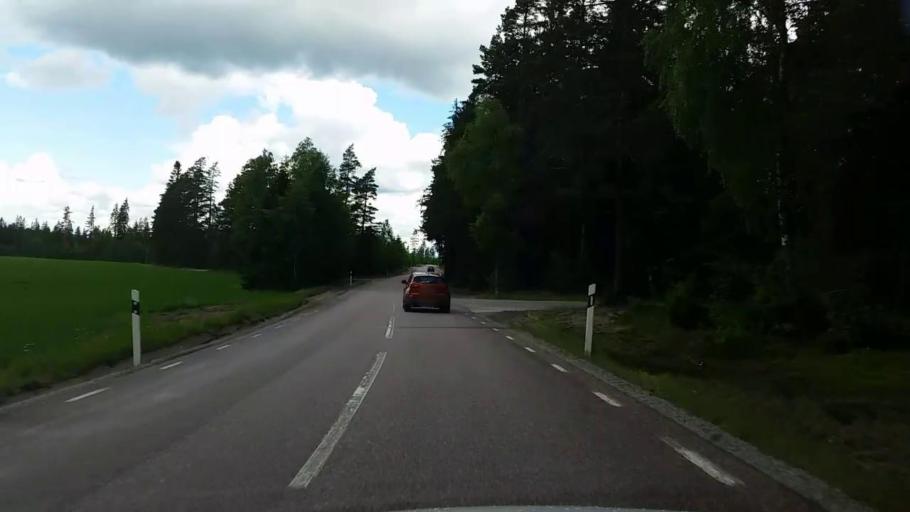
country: SE
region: Vaestmanland
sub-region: Fagersta Kommun
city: Fagersta
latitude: 59.8860
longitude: 15.8309
